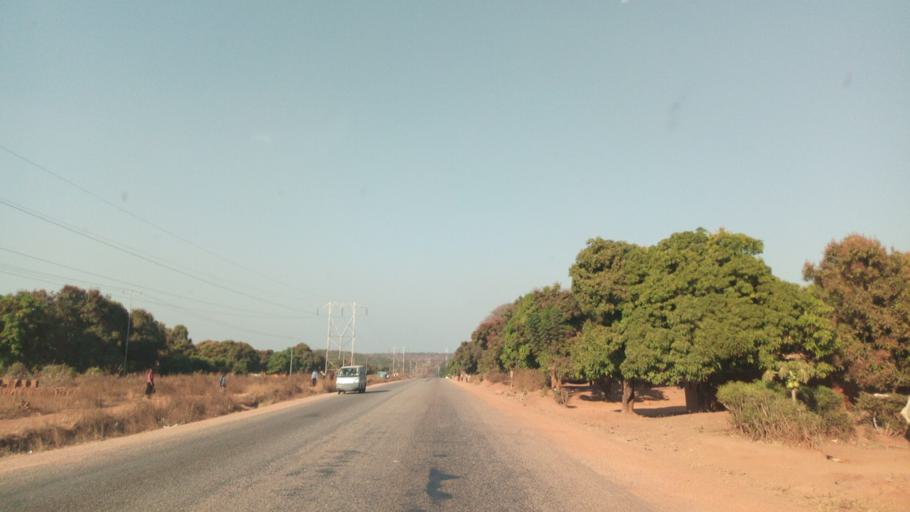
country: CD
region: Katanga
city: Likasi
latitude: -11.0009
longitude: 26.8783
